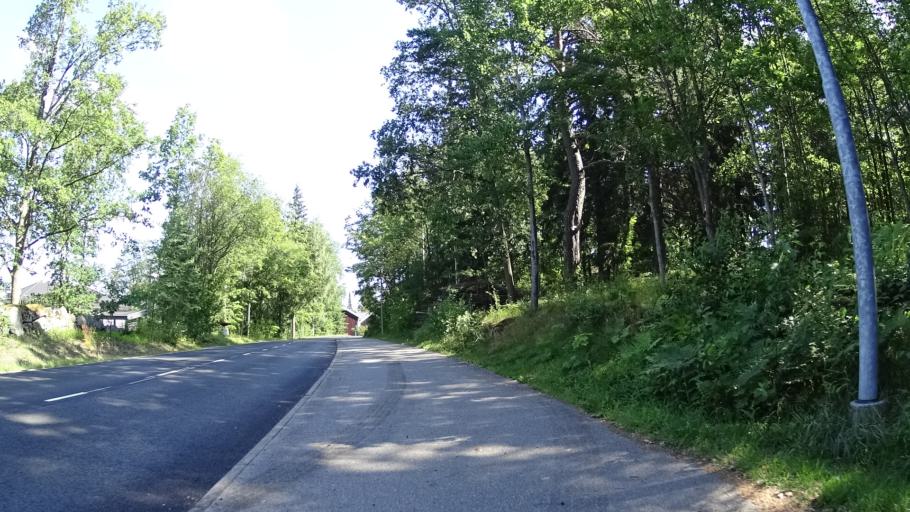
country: FI
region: Uusimaa
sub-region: Helsinki
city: Tuusula
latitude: 60.4110
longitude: 25.0312
